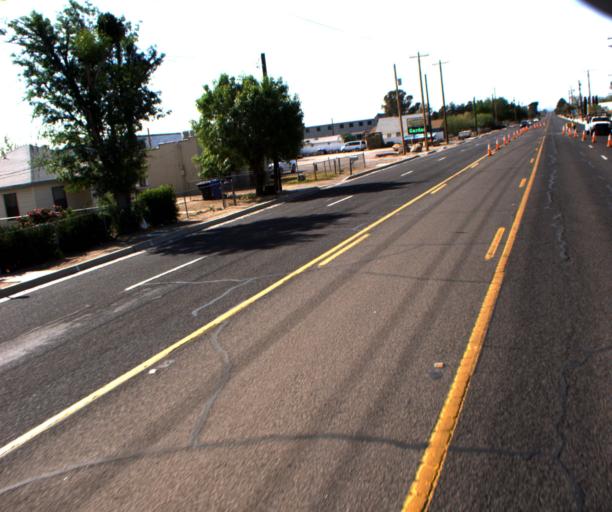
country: US
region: Arizona
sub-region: Graham County
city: Safford
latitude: 32.8220
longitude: -109.7077
